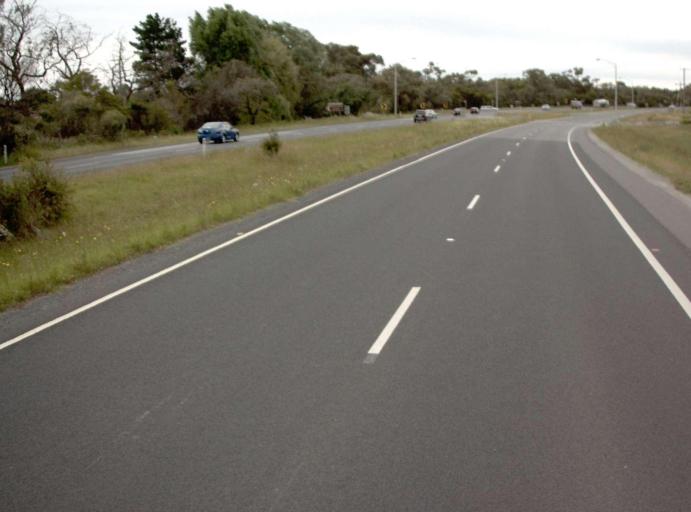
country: AU
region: Victoria
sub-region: Casey
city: Junction Village
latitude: -38.1304
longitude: 145.2930
